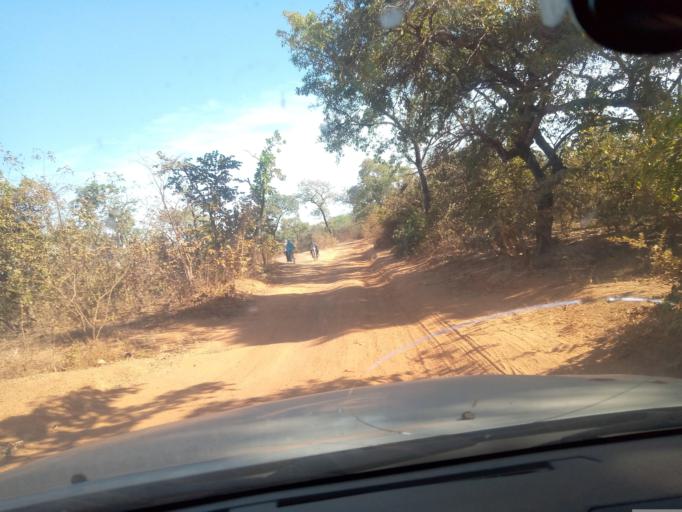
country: ML
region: Sikasso
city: Sikasso
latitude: 11.4690
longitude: -5.3274
